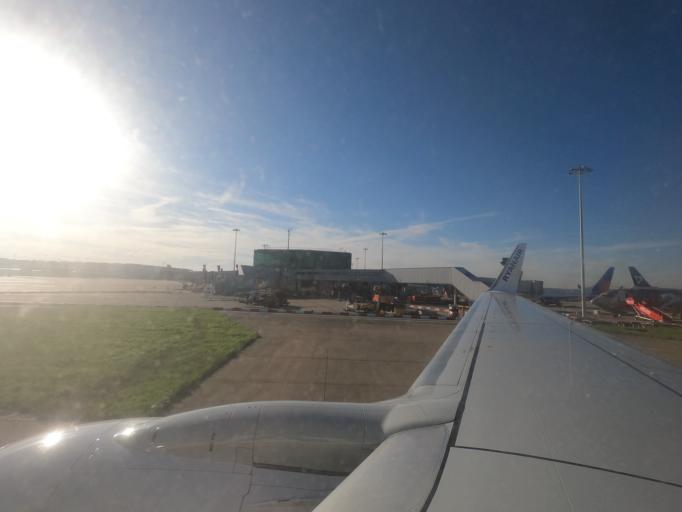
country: GB
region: England
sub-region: Essex
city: Takeley
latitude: 51.8908
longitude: 0.2515
